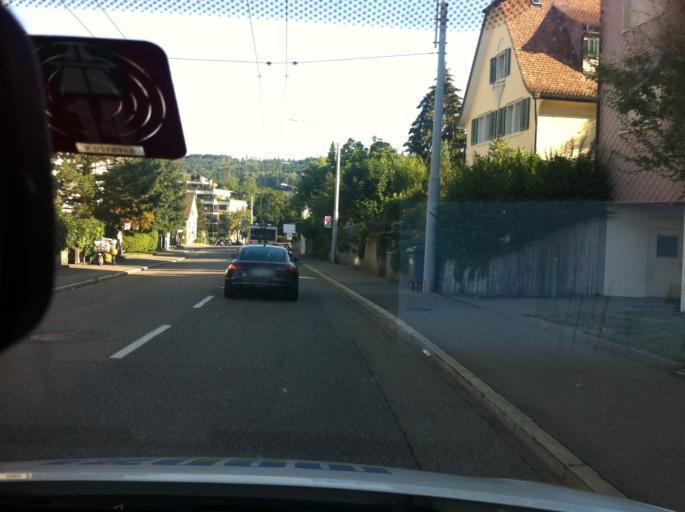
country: CH
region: Zurich
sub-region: Bezirk Zuerich
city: Zuerich (Kreis 7) / Witikon
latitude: 47.3587
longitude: 8.5956
